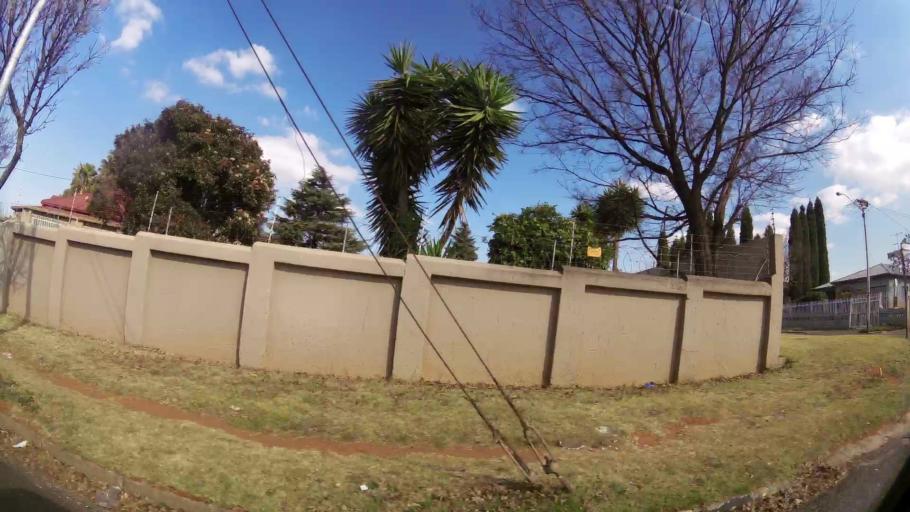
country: ZA
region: Gauteng
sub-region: Ekurhuleni Metropolitan Municipality
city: Germiston
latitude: -26.1819
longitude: 28.1683
